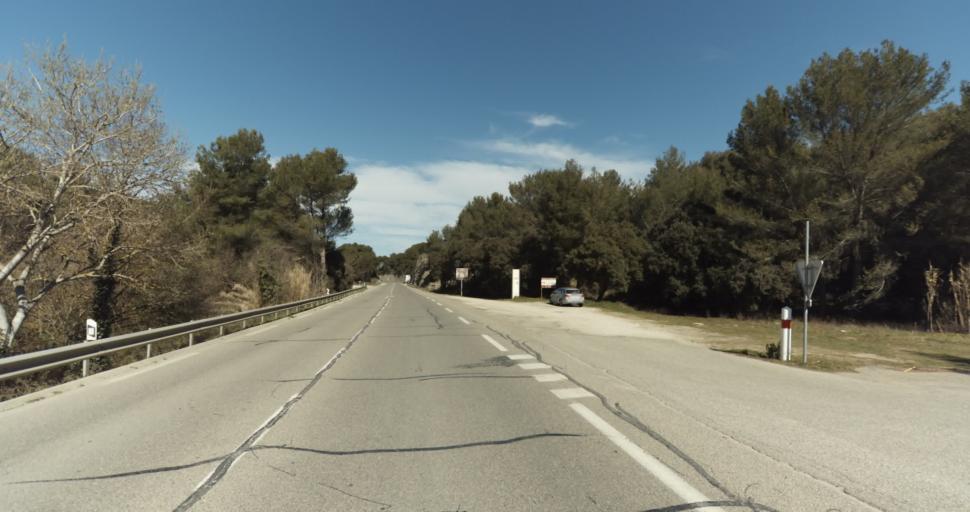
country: FR
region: Provence-Alpes-Cote d'Azur
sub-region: Departement des Bouches-du-Rhone
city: Lambesc
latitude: 43.6500
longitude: 5.2738
